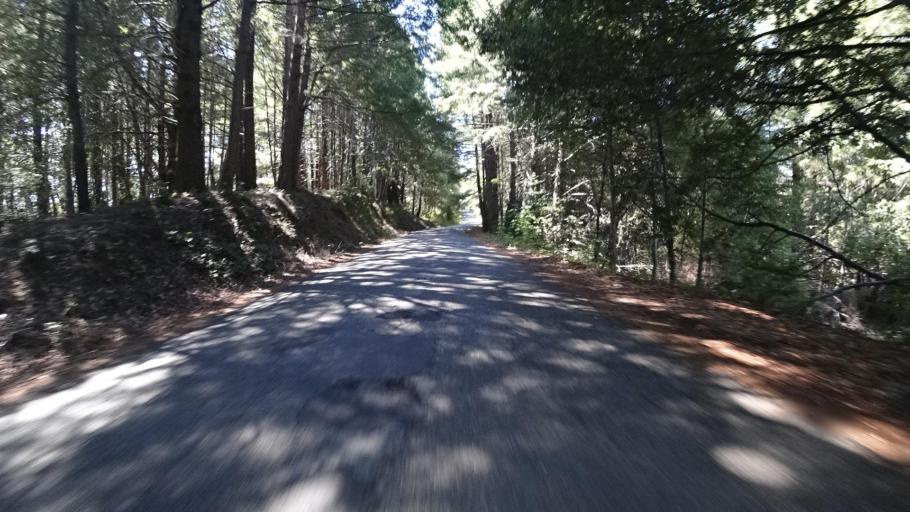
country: US
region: California
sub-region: Humboldt County
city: Redway
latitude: 40.1808
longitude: -124.0886
